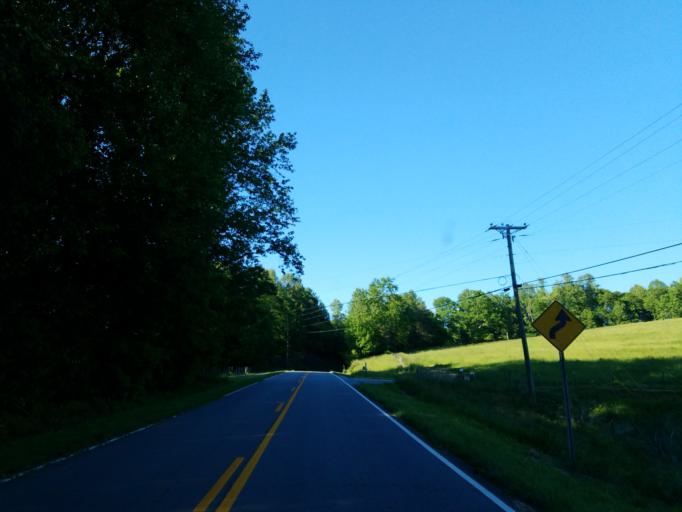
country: US
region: Georgia
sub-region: Gilmer County
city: Ellijay
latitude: 34.6867
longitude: -84.3145
